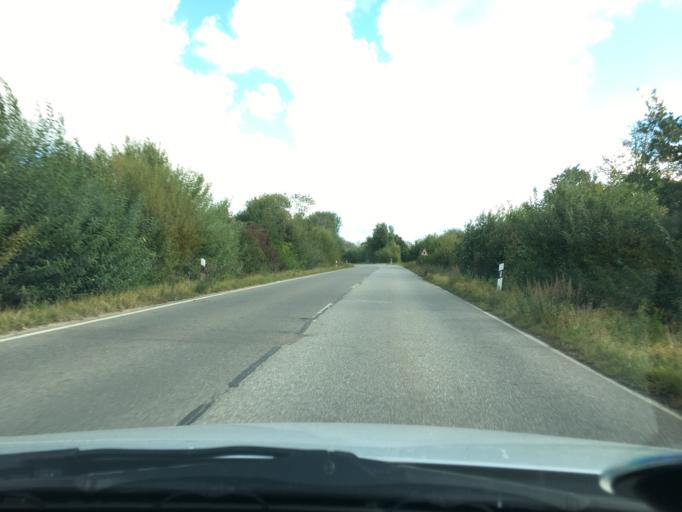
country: DE
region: Schleswig-Holstein
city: Wendtorf
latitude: 54.4156
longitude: 10.2888
